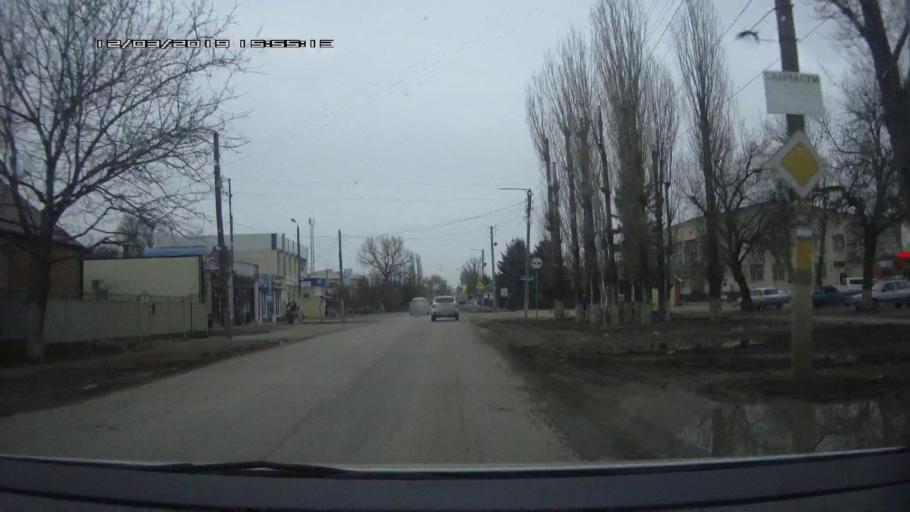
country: RU
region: Rostov
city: Novobataysk
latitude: 46.8954
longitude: 39.7793
